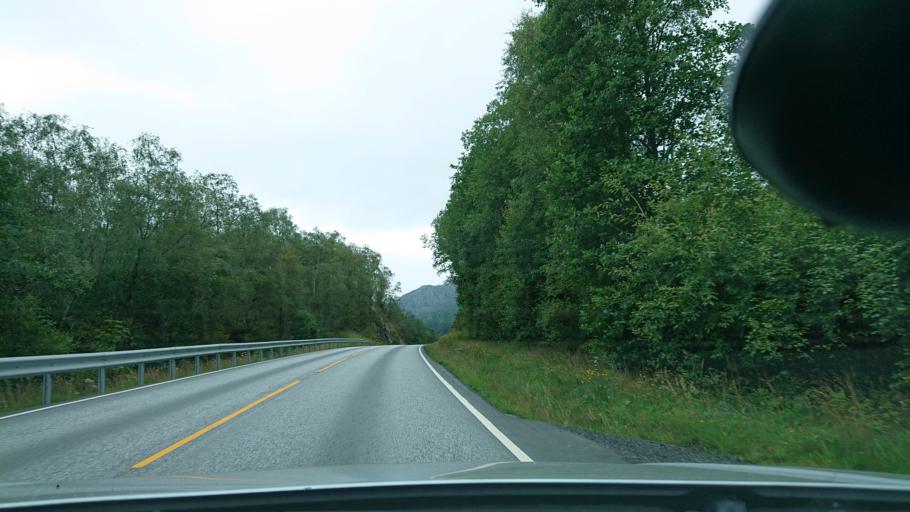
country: NO
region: Rogaland
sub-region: Hjelmeland
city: Hjelmelandsvagen
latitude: 59.1672
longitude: 6.1569
